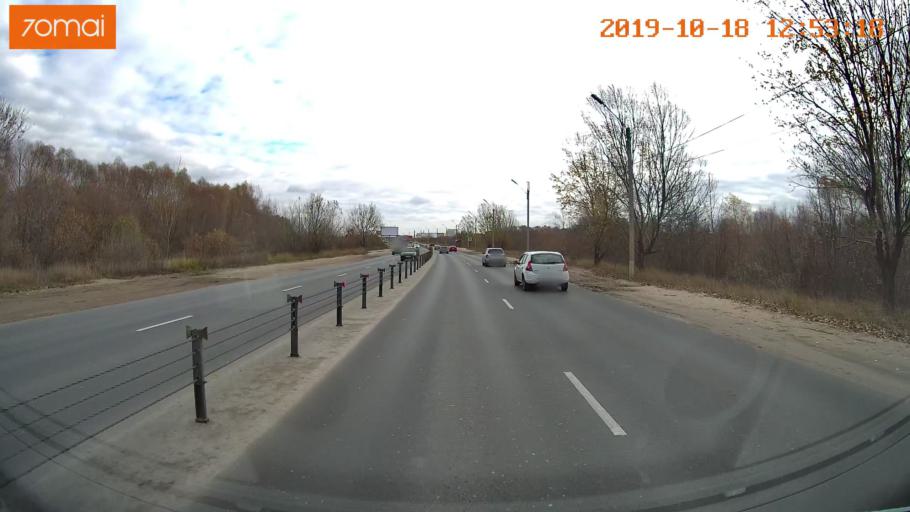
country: RU
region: Rjazan
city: Ryazan'
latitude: 54.6454
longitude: 39.7047
